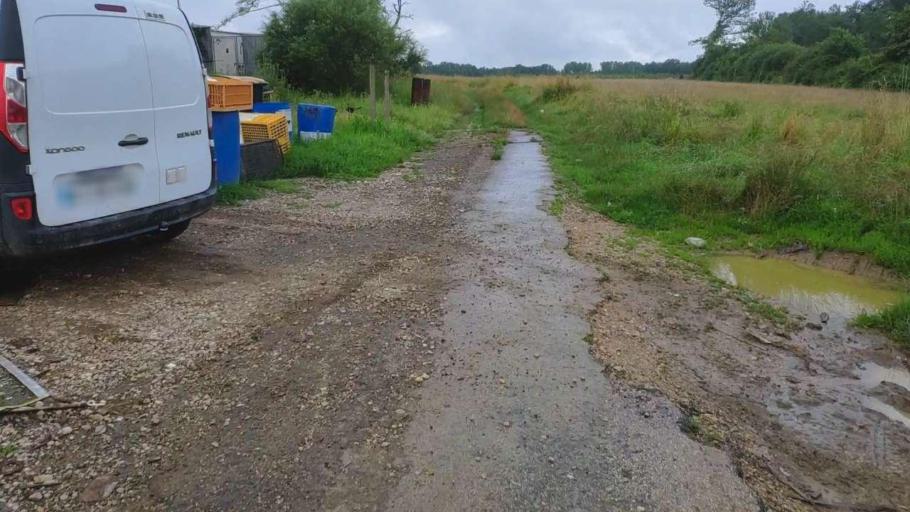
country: FR
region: Franche-Comte
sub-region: Departement du Jura
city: Mont-sous-Vaudrey
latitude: 46.8628
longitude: 5.5355
